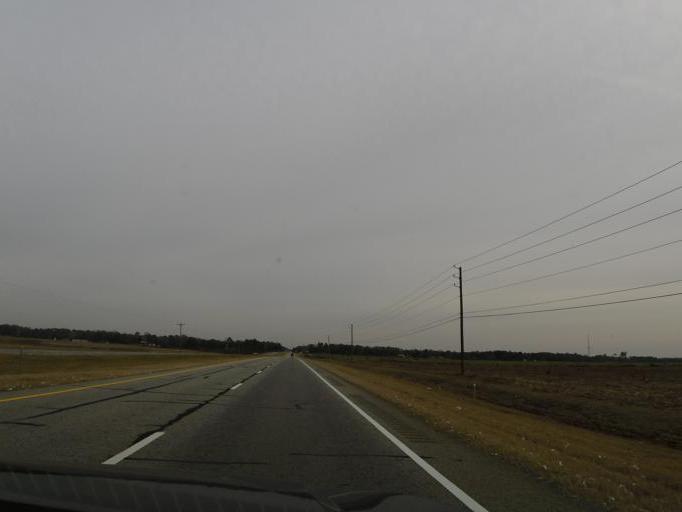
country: US
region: Georgia
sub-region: Decatur County
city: Bainbridge
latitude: 30.9361
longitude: -84.6579
